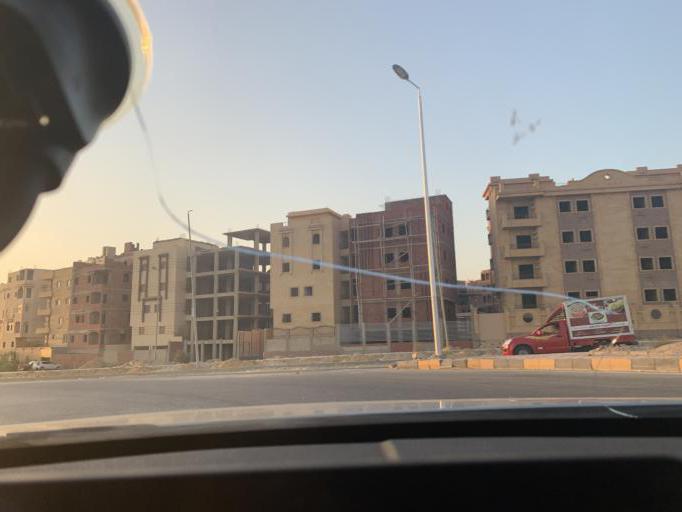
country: EG
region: Muhafazat al Qahirah
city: Halwan
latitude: 29.9756
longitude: 31.4726
